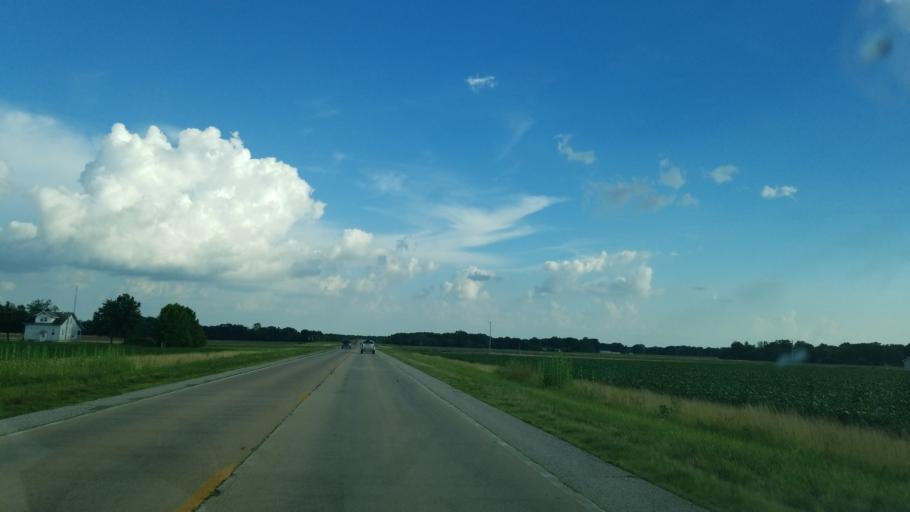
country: US
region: Illinois
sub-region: Marion County
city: Sandoval
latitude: 38.5927
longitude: -89.1084
